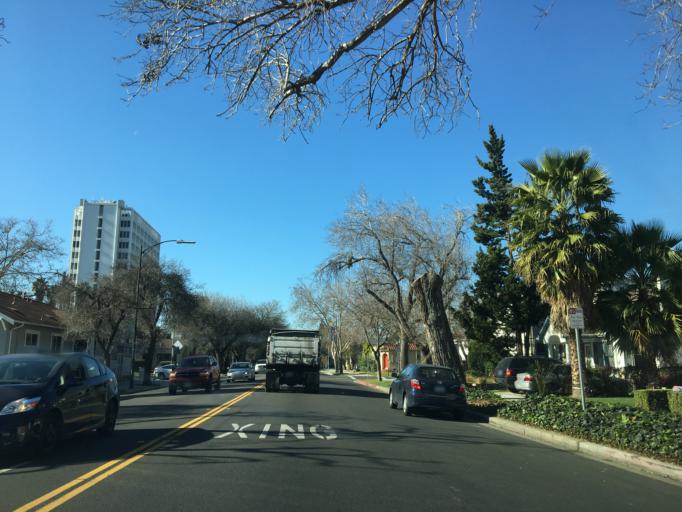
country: US
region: California
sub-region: Santa Clara County
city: San Jose
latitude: 37.3500
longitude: -121.8986
